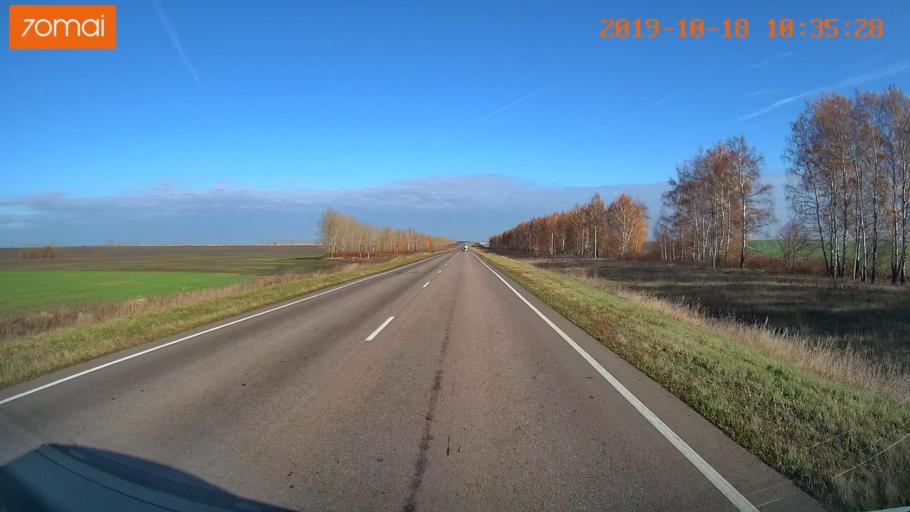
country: RU
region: Tula
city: Kurkino
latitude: 53.5336
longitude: 38.6201
